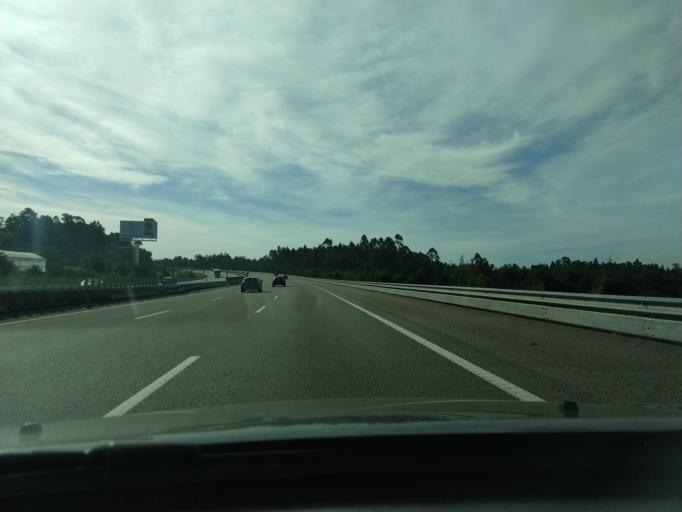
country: PT
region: Aveiro
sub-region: Santa Maria da Feira
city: Feira
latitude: 40.8914
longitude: -8.5684
